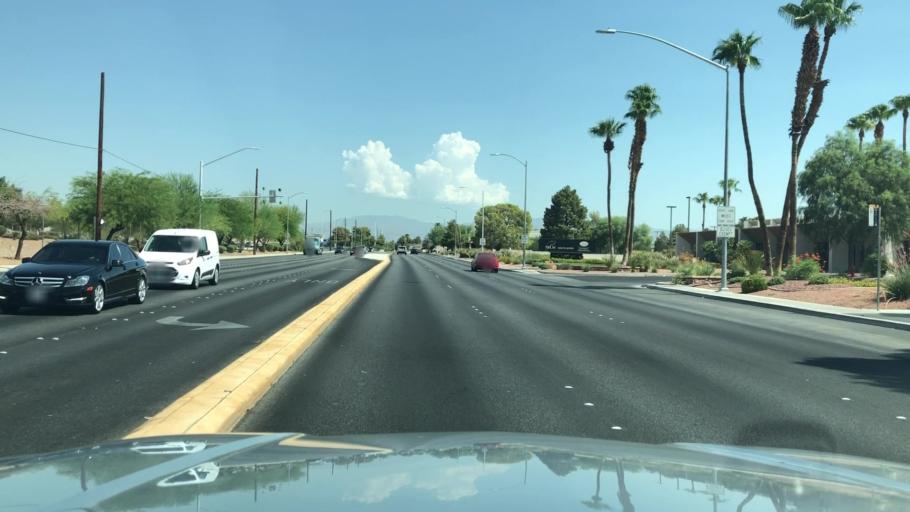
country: US
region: Nevada
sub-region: Clark County
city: Spring Valley
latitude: 36.1521
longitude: -115.2255
